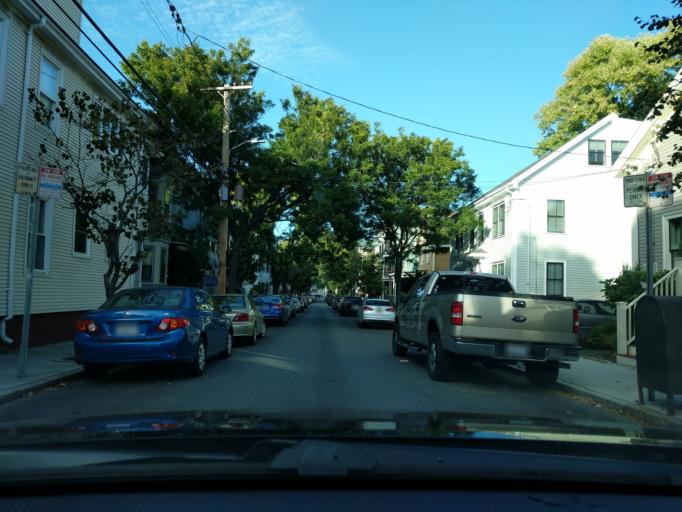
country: US
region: Massachusetts
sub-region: Middlesex County
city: Cambridge
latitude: 42.3711
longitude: -71.1010
